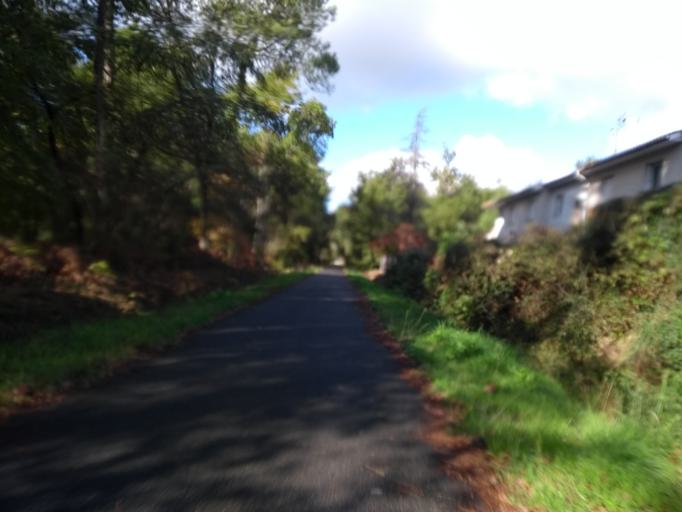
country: FR
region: Aquitaine
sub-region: Departement de la Gironde
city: Saint-Aubin-de-Medoc
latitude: 44.7823
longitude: -0.6948
